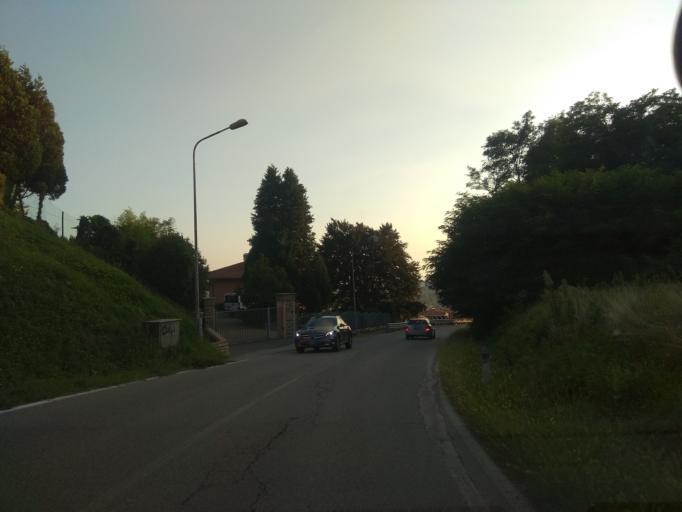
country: IT
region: Piedmont
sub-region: Provincia di Novara
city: Romagnano Sesia
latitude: 45.6387
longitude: 8.3864
